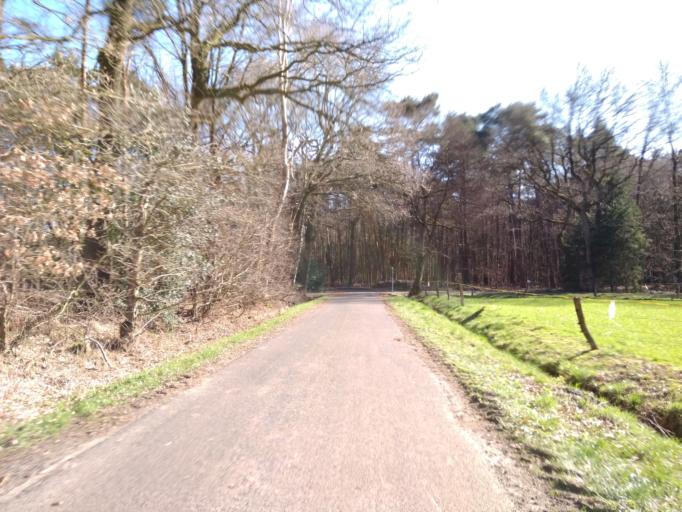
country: DE
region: North Rhine-Westphalia
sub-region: Regierungsbezirk Dusseldorf
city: Hunxe
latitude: 51.6363
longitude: 6.8293
